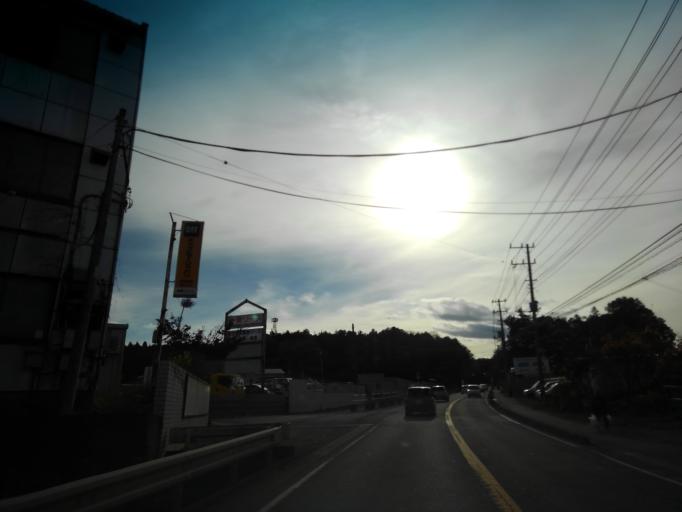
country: JP
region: Saitama
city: Hanno
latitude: 35.8780
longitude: 139.3362
